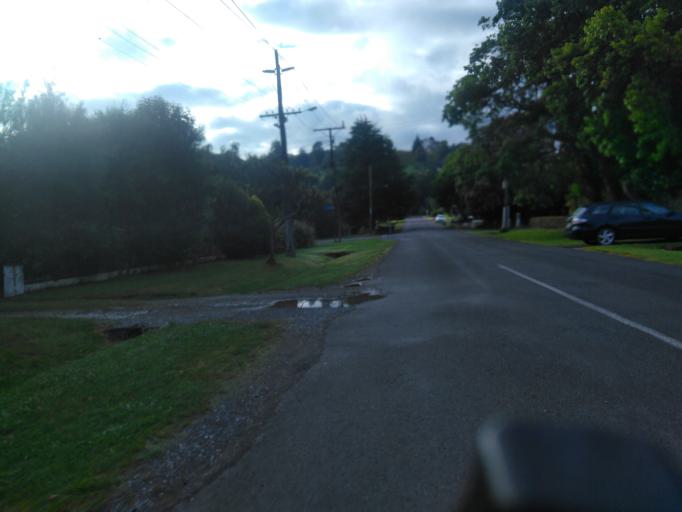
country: NZ
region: Gisborne
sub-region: Gisborne District
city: Gisborne
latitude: -38.6470
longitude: 178.0215
